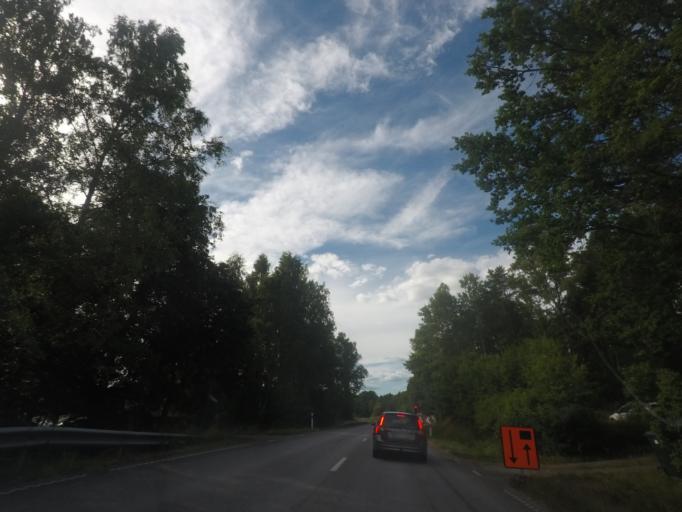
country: SE
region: Stockholm
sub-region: Norrtalje Kommun
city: Skanninge
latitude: 59.9023
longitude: 18.5922
